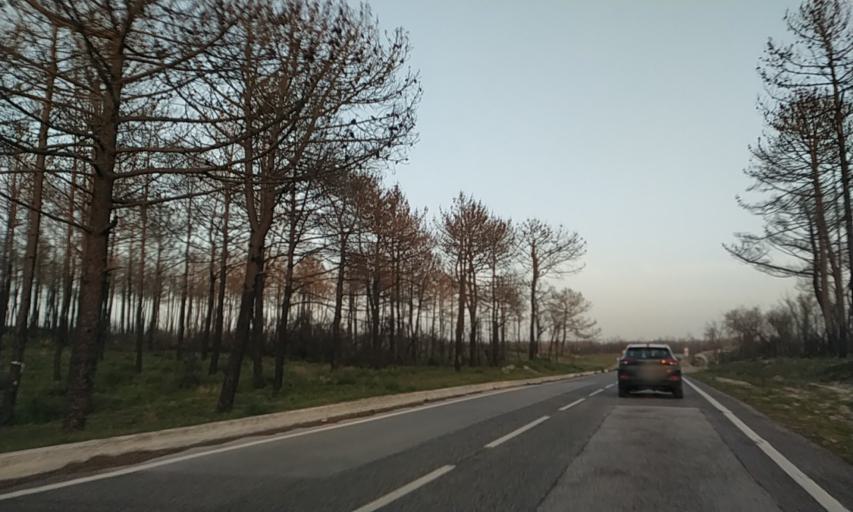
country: PT
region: Leiria
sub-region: Marinha Grande
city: Marinha Grande
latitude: 39.7506
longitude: -9.0128
